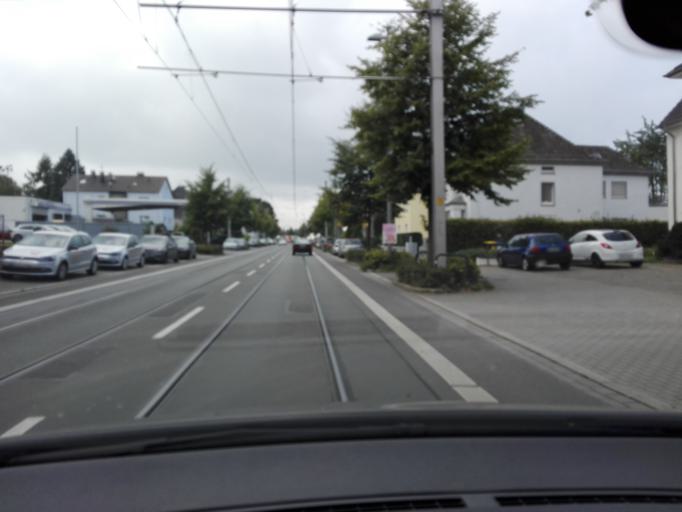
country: DE
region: North Rhine-Westphalia
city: Lanstrop
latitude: 51.5280
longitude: 7.5802
